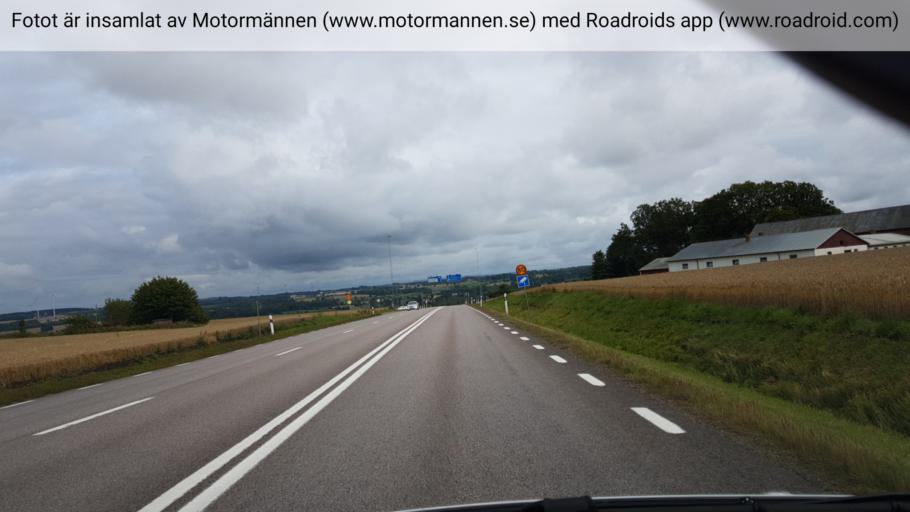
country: SE
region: Vaestra Goetaland
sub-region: Falkopings Kommun
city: Falkoeping
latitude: 58.1417
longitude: 13.6317
